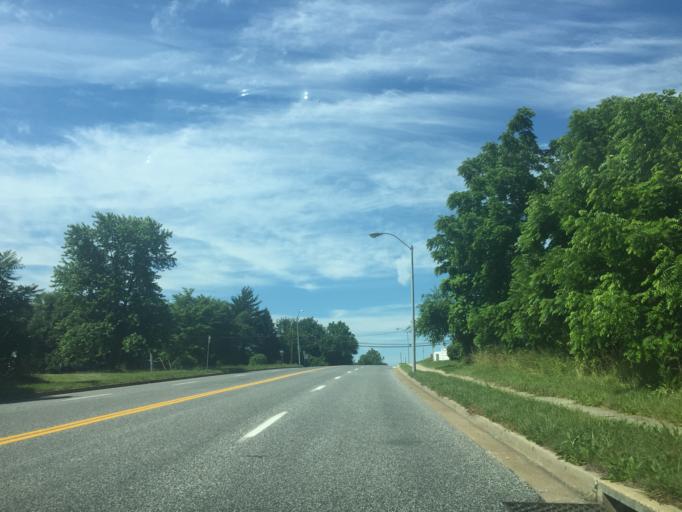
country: US
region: Maryland
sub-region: Baltimore County
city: Rossville
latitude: 39.3316
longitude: -76.4797
